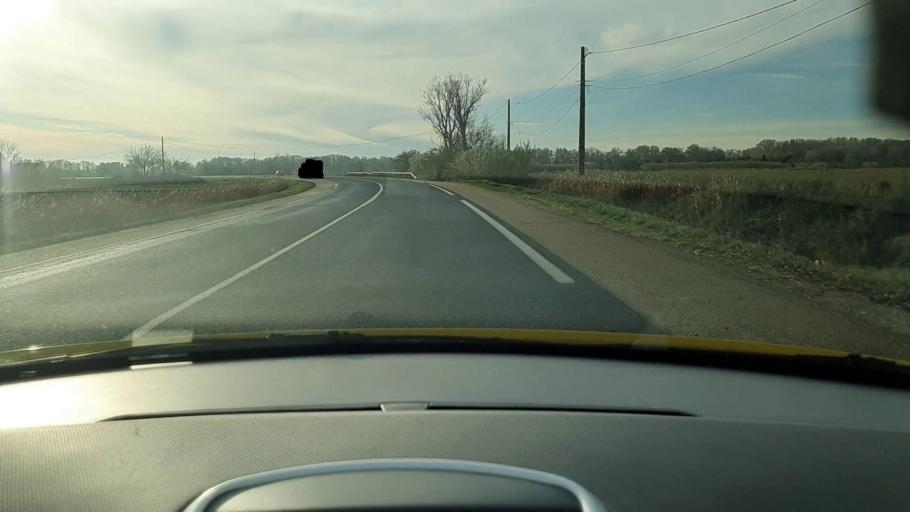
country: FR
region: Languedoc-Roussillon
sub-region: Departement du Gard
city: Bellegarde
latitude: 43.7115
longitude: 4.5490
